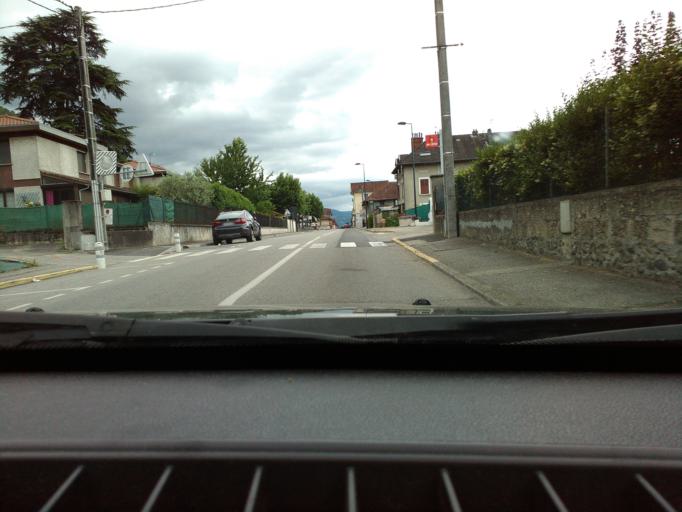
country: FR
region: Rhone-Alpes
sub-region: Departement de l'Isere
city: Froges
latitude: 45.2599
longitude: 5.9099
